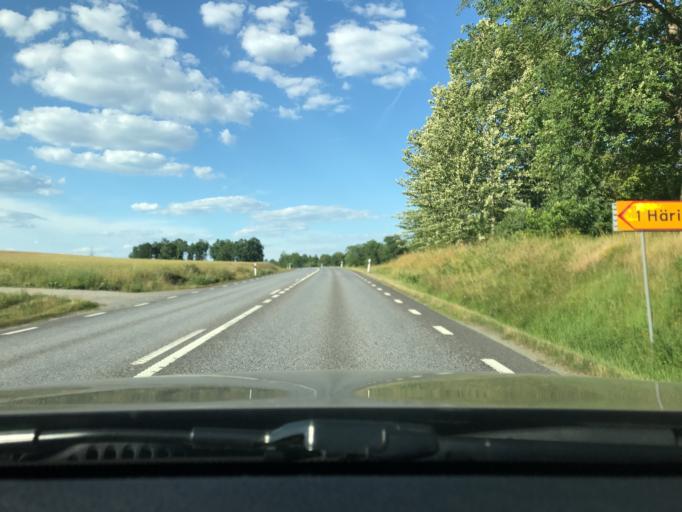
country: SE
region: Kronoberg
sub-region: Vaxjo Kommun
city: Gemla
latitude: 56.8397
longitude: 14.7081
